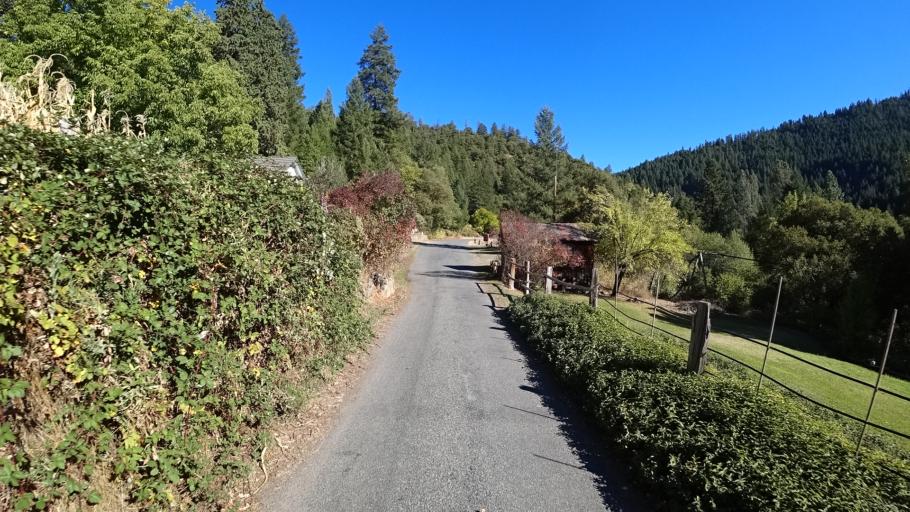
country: US
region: California
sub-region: Siskiyou County
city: Happy Camp
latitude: 41.2998
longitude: -123.1343
